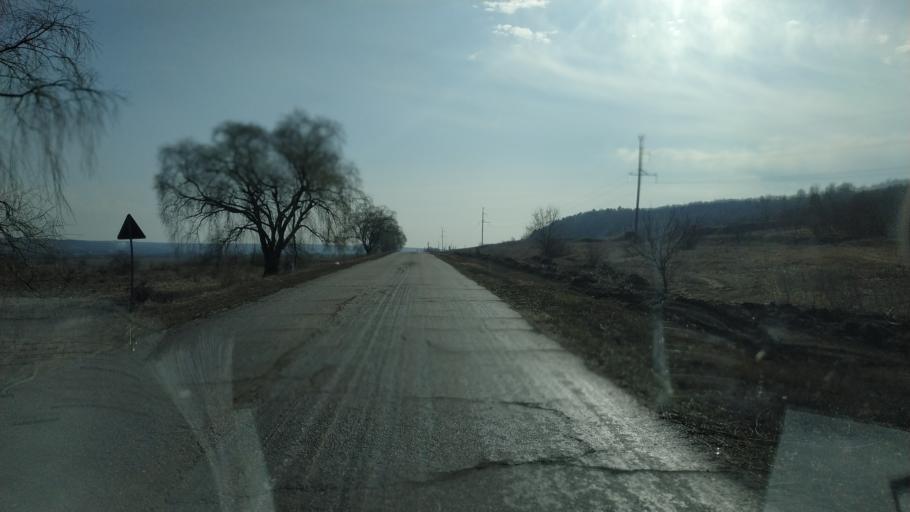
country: MD
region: Chisinau
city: Singera
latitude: 46.7035
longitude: 29.0509
